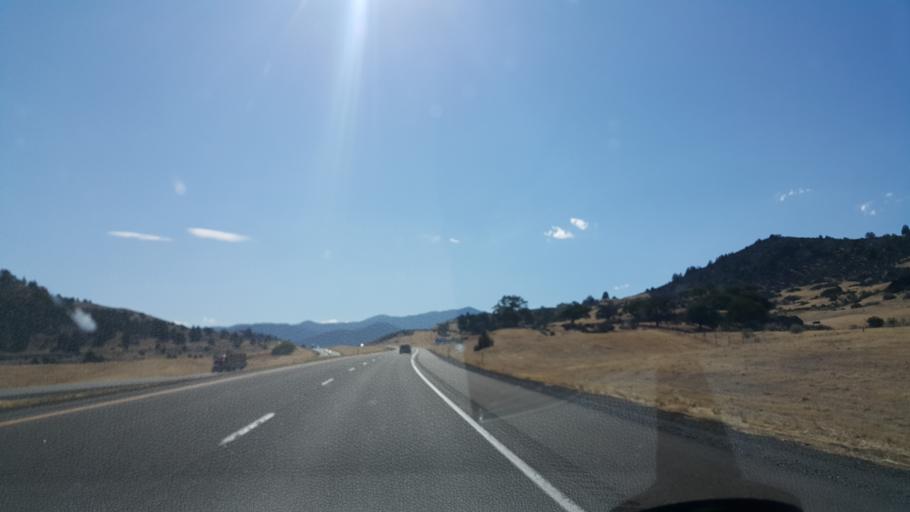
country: US
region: California
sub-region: Siskiyou County
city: Yreka
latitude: 41.7565
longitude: -122.6016
